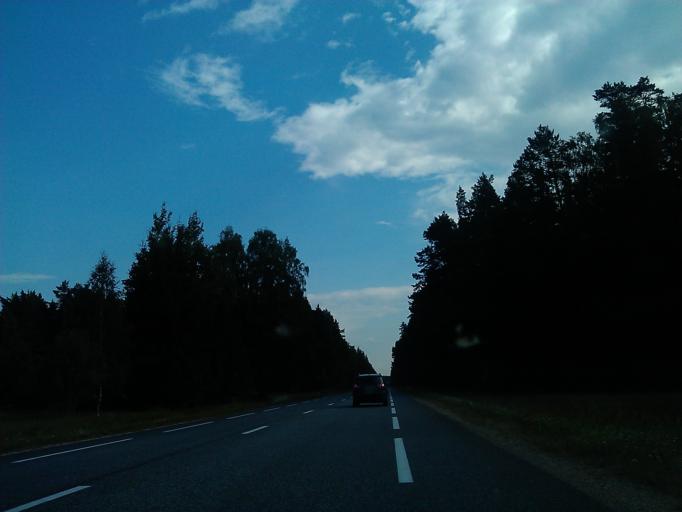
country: LV
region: Saulkrastu
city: Saulkrasti
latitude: 57.3832
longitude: 24.4302
